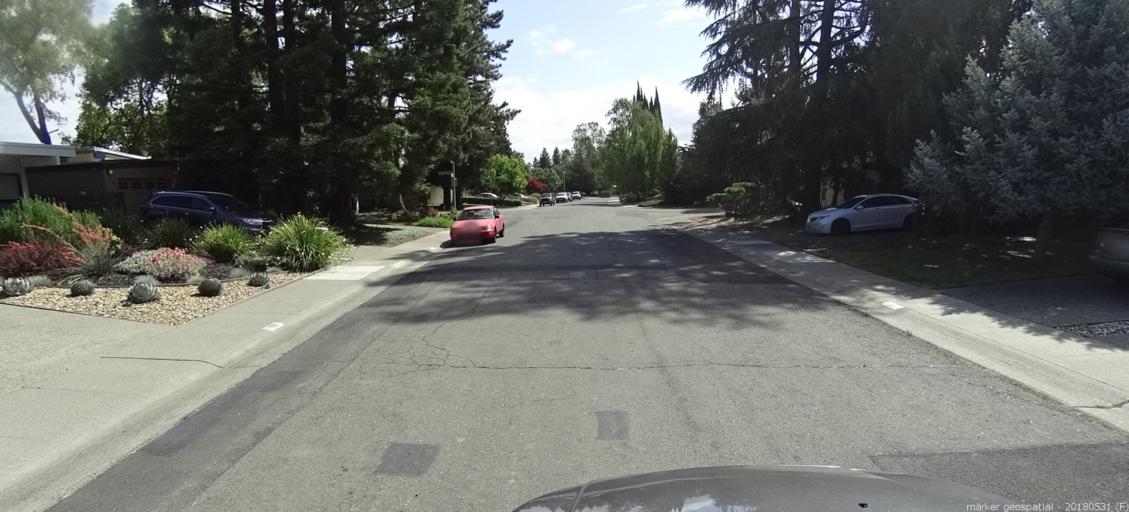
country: US
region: California
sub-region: Sacramento County
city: Sacramento
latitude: 38.6164
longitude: -121.5009
